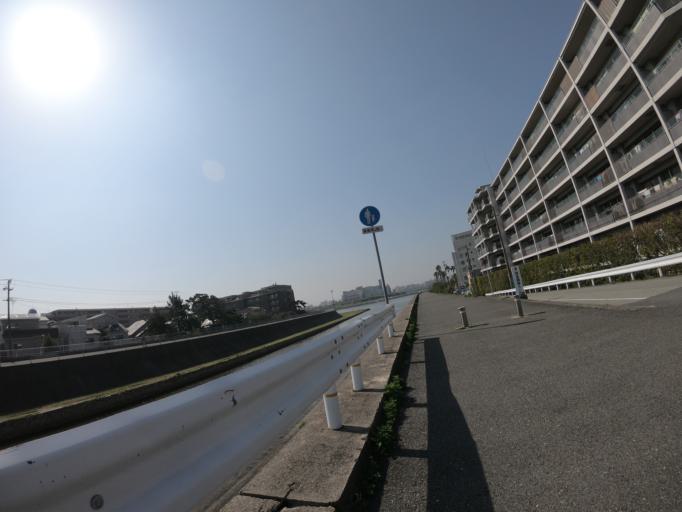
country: JP
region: Hyogo
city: Nishinomiya-hama
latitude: 34.7267
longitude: 135.3287
